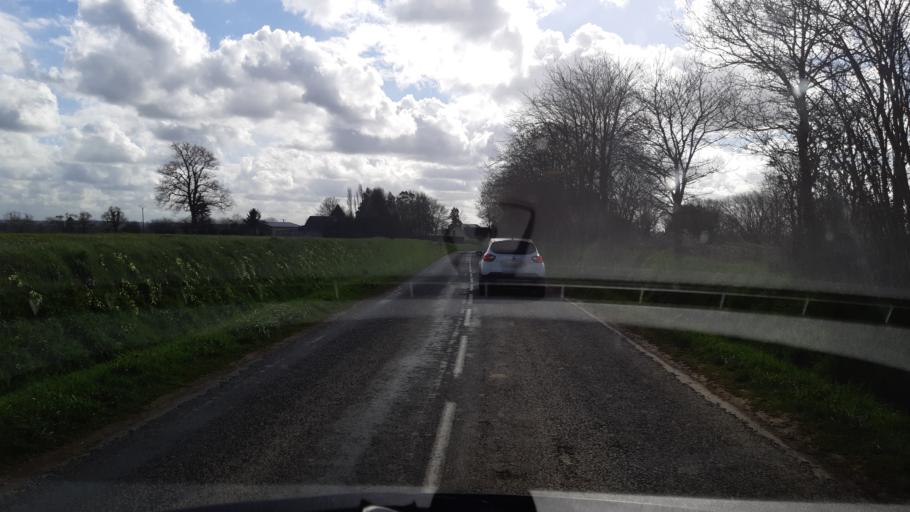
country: FR
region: Lower Normandy
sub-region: Departement de la Manche
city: Percy
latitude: 49.0157
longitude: -1.1645
